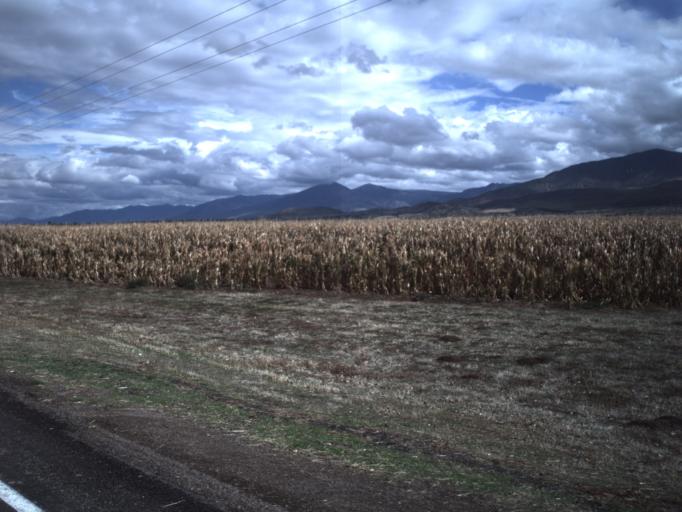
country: US
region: Utah
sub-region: Millard County
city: Fillmore
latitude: 38.8617
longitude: -112.4185
